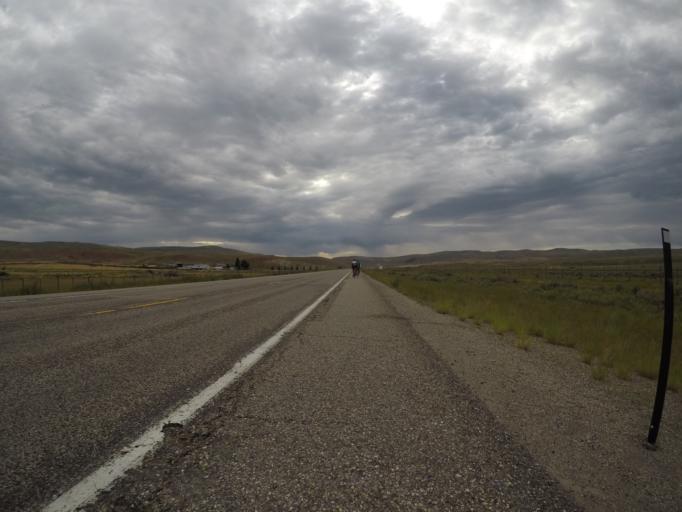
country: US
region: Utah
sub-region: Rich County
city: Randolph
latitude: 41.8250
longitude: -110.9124
